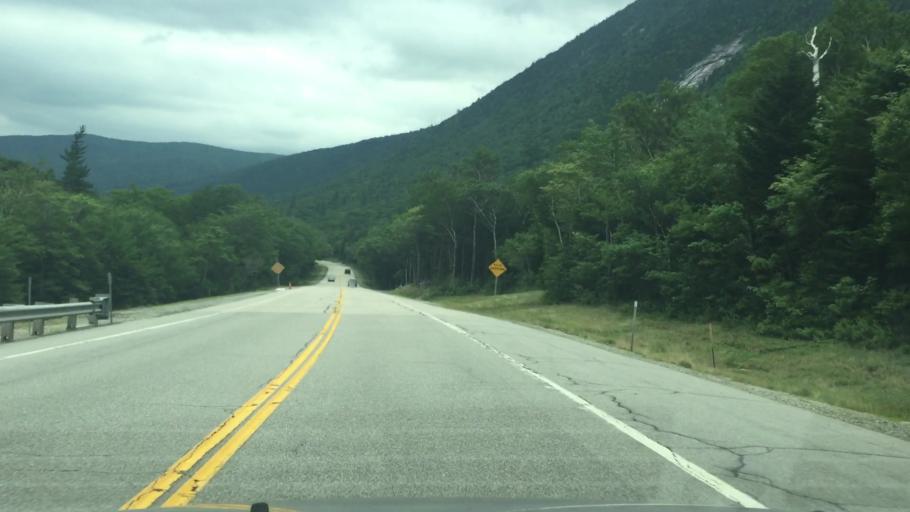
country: US
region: New Hampshire
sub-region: Grafton County
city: Deerfield
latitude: 44.1971
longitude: -71.4071
